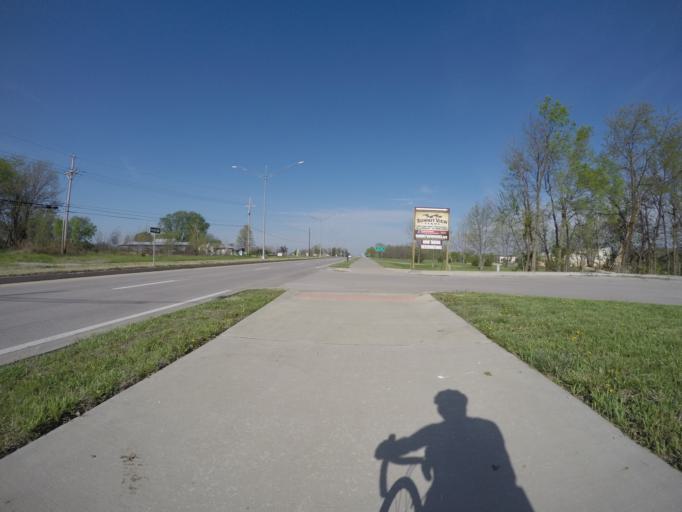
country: US
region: Missouri
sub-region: Cass County
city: Raymore
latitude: 38.8543
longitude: -94.4315
